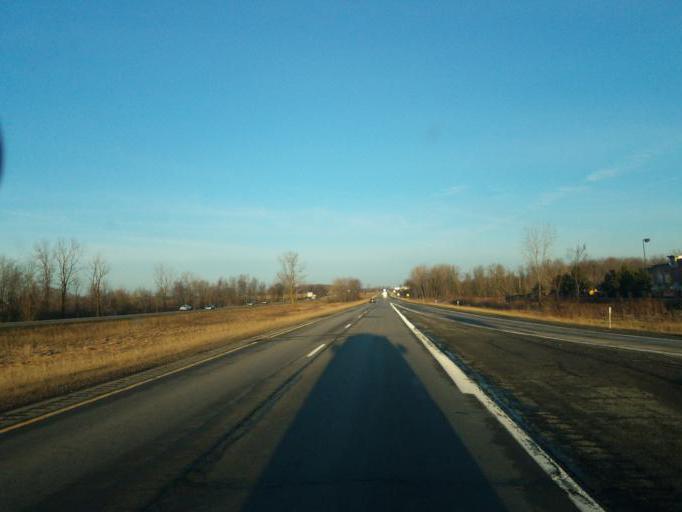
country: US
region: Michigan
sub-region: Livingston County
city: Fowlerville
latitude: 42.6466
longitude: -84.0759
